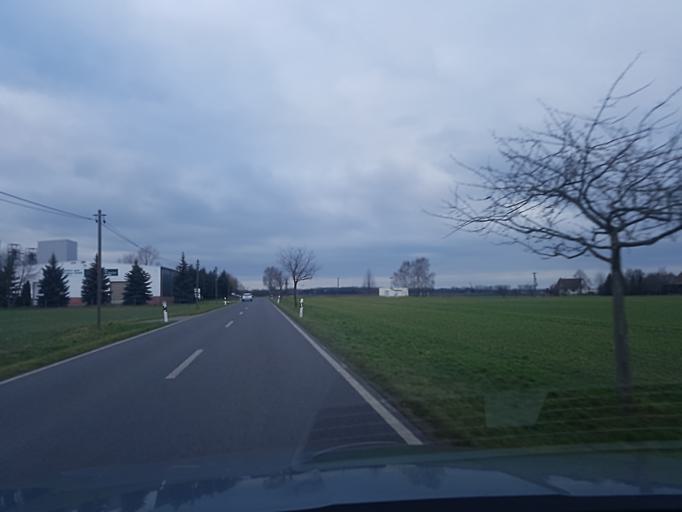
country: DE
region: Brandenburg
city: Sonnewalde
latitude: 51.6910
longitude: 13.6748
